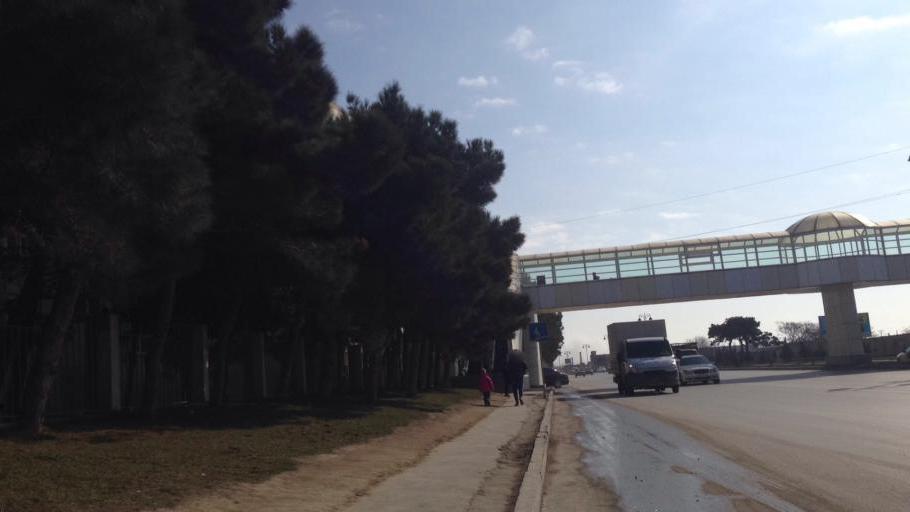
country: AZ
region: Baki
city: Baku
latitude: 40.3749
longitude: 49.9248
